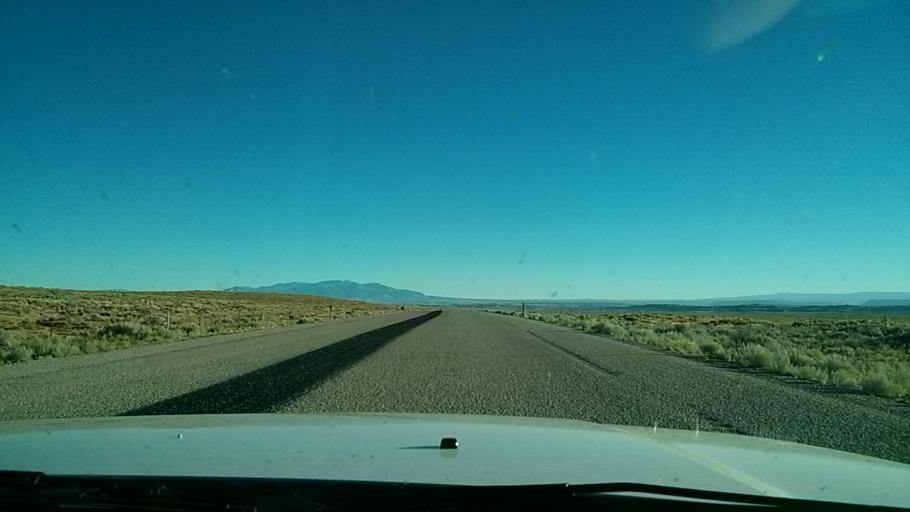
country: US
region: Utah
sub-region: Emery County
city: Ferron
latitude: 38.5628
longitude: -110.6088
